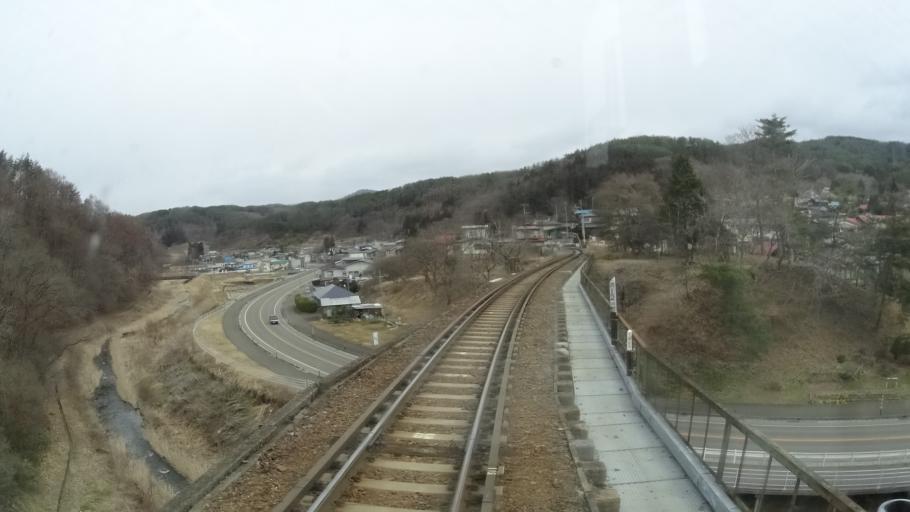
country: JP
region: Iwate
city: Tono
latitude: 39.3471
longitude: 141.3495
